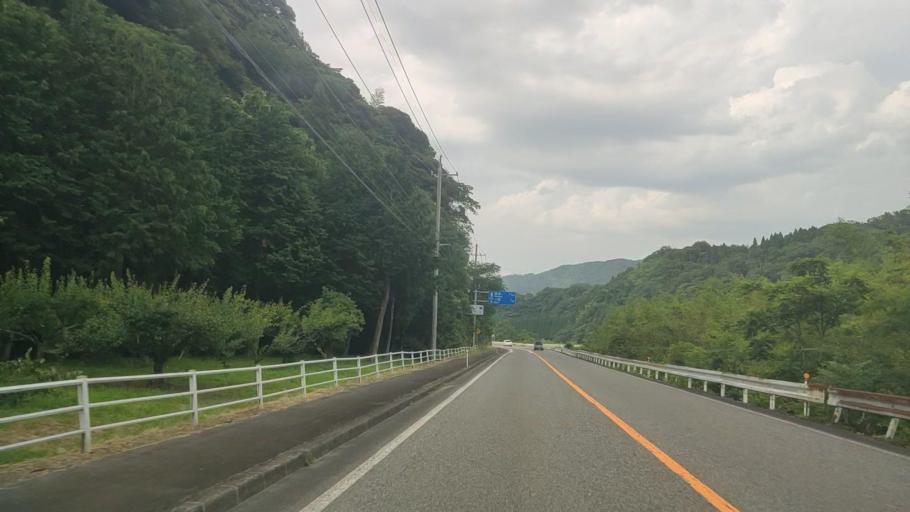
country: JP
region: Tottori
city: Kurayoshi
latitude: 35.3542
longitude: 133.8448
